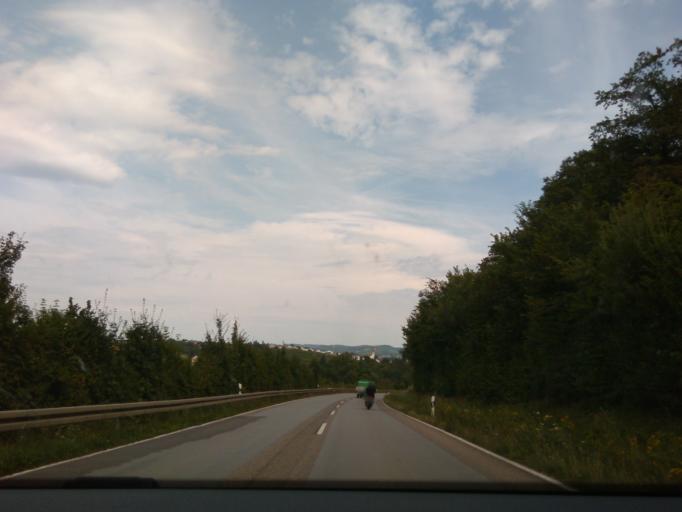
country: DE
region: Baden-Wuerttemberg
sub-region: Regierungsbezirk Stuttgart
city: Ilsfeld
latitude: 49.0522
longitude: 9.2198
